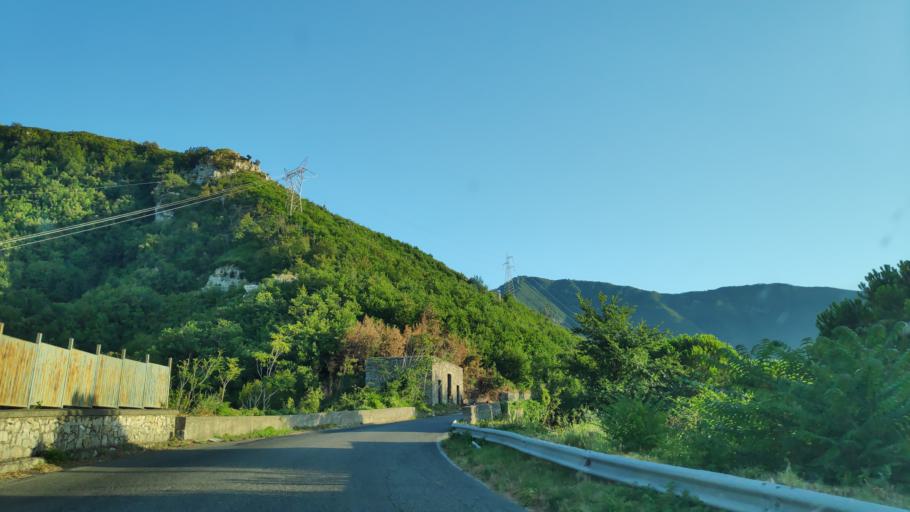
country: IT
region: Campania
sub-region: Provincia di Salerno
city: Corbara
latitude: 40.7222
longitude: 14.6054
